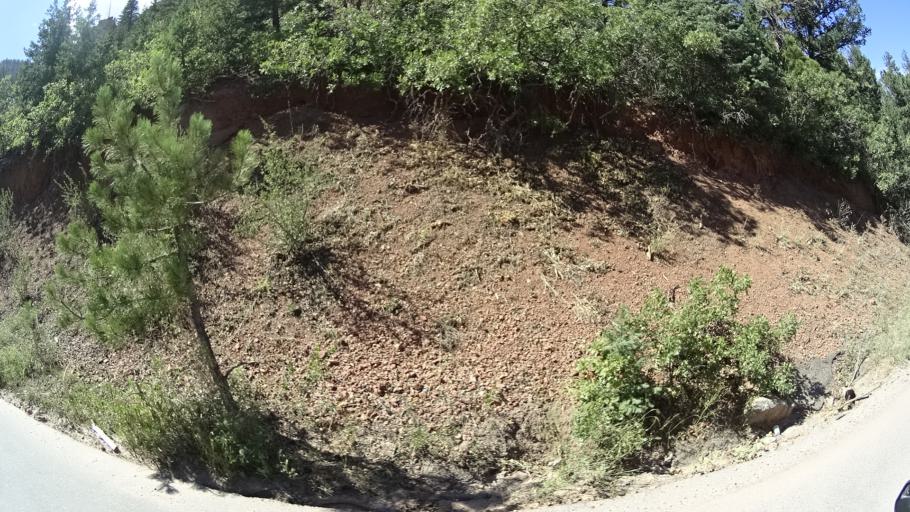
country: US
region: Colorado
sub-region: El Paso County
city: Colorado Springs
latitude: 38.7777
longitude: -104.8636
